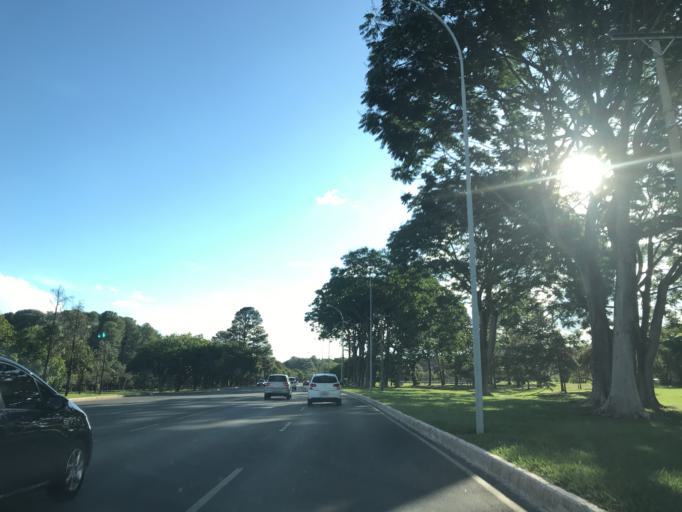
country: BR
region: Federal District
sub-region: Brasilia
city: Brasilia
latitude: -15.8015
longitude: -47.9171
